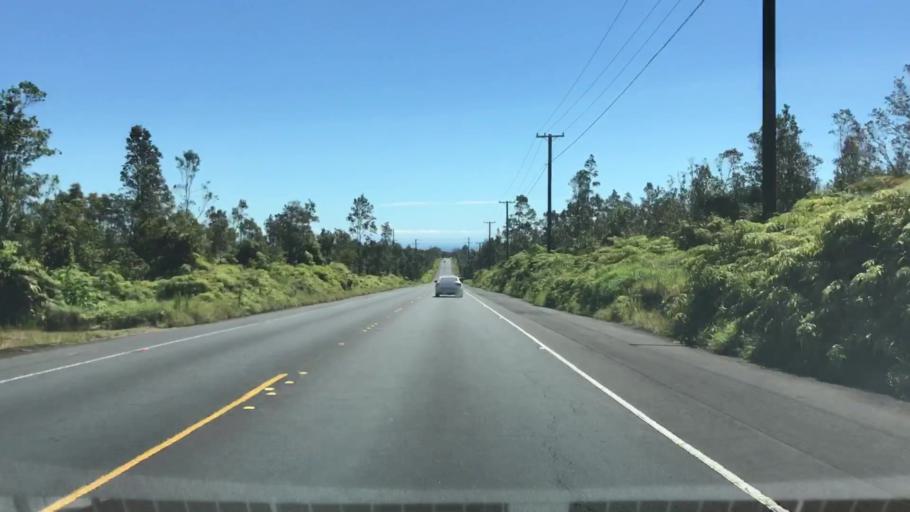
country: US
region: Hawaii
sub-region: Hawaii County
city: Volcano
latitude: 19.4517
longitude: -155.1892
